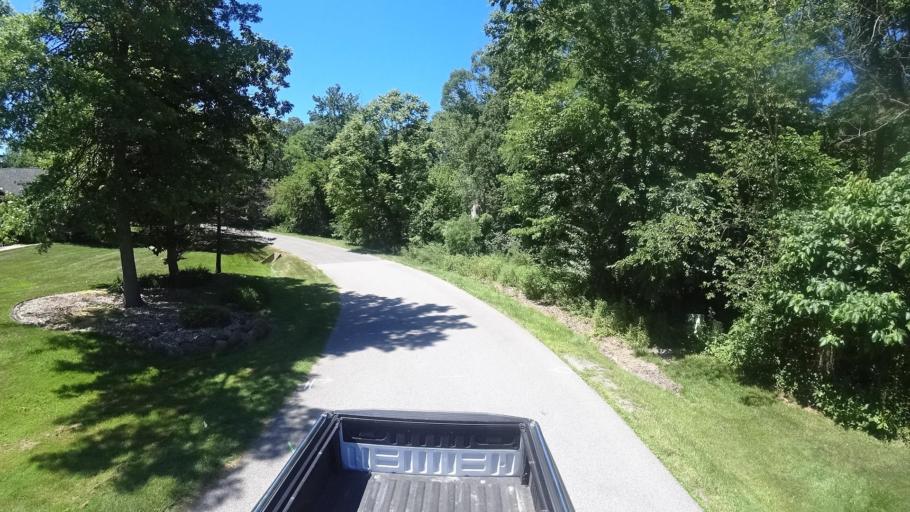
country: US
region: Indiana
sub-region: Porter County
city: Porter
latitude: 41.6350
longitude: -87.0817
